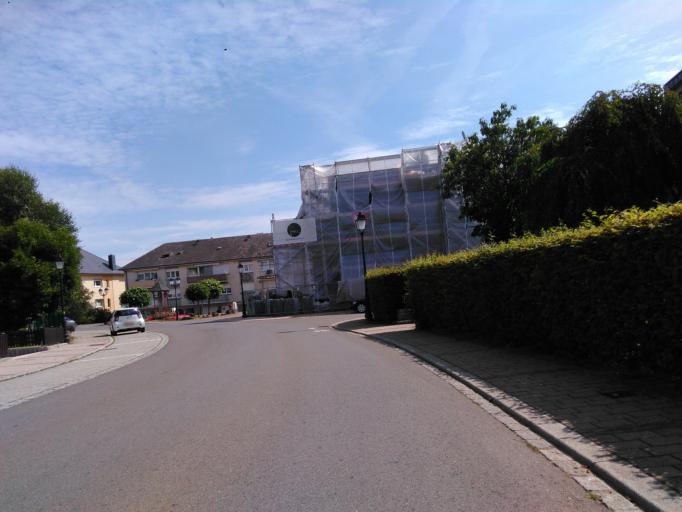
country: LU
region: Luxembourg
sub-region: Canton de Luxembourg
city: Hesperange
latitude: 49.5666
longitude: 6.1541
